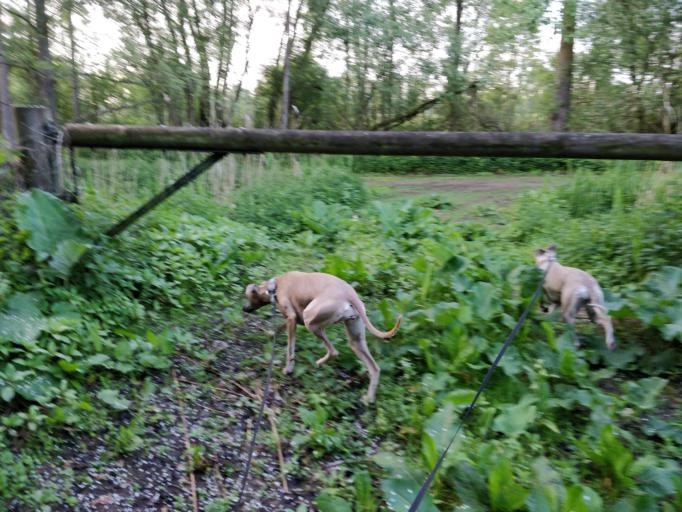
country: BE
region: Flanders
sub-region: Provincie Antwerpen
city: Rumst
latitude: 51.0768
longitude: 4.4362
